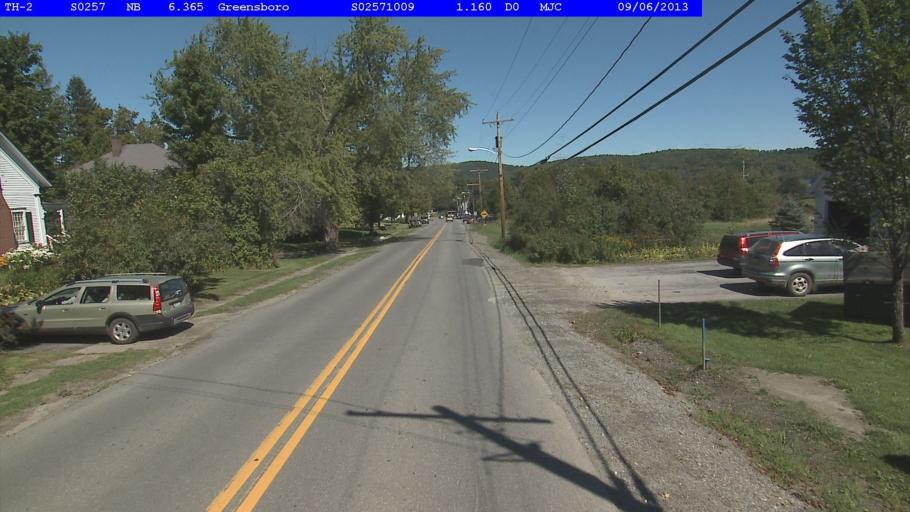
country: US
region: Vermont
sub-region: Caledonia County
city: Hardwick
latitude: 44.5733
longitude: -72.2974
